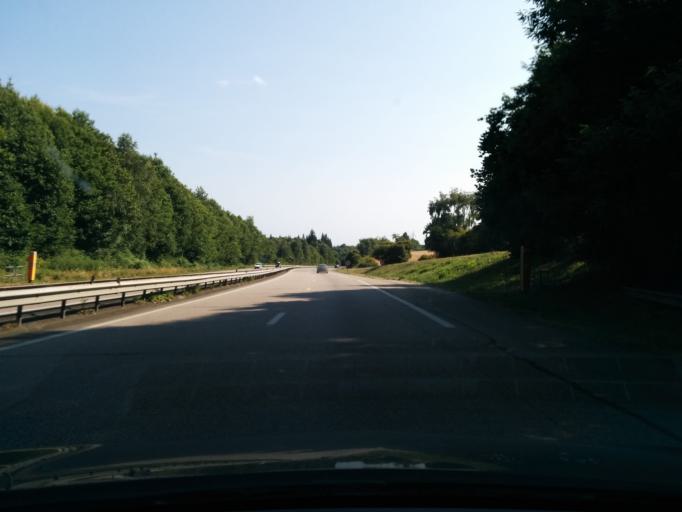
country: FR
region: Limousin
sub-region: Departement de la Haute-Vienne
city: Bonnac-la-Cote
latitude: 45.9380
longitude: 1.3045
